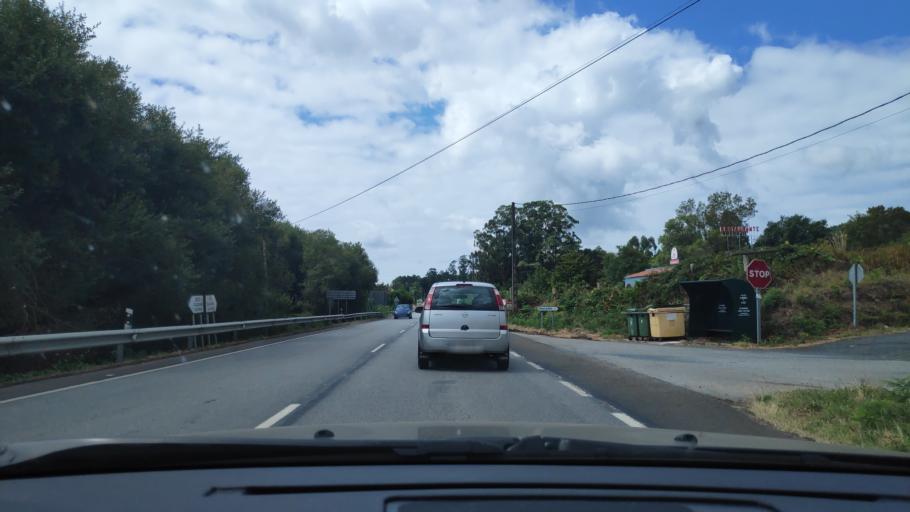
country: ES
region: Galicia
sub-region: Provincia de Pontevedra
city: Portas
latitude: 42.5851
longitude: -8.6946
